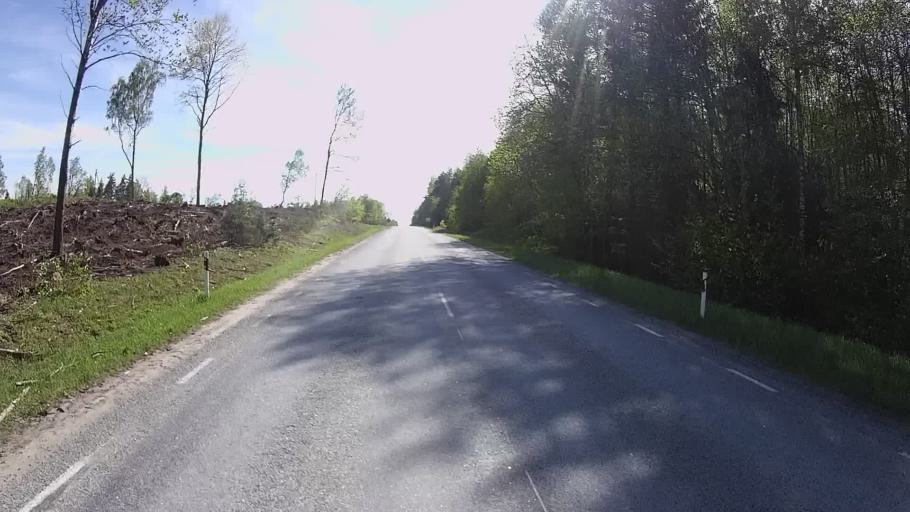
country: EE
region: Vorumaa
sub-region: Antsla vald
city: Vana-Antsla
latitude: 57.9870
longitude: 26.4804
